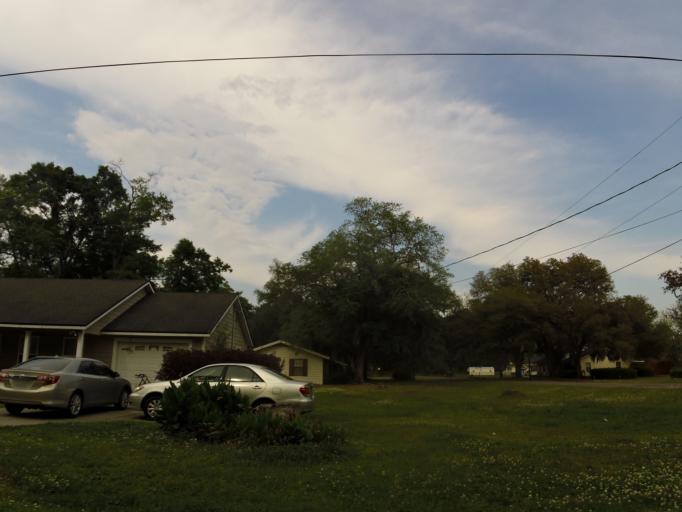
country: US
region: Florida
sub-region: Nassau County
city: Hilliard
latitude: 30.6896
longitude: -81.9234
